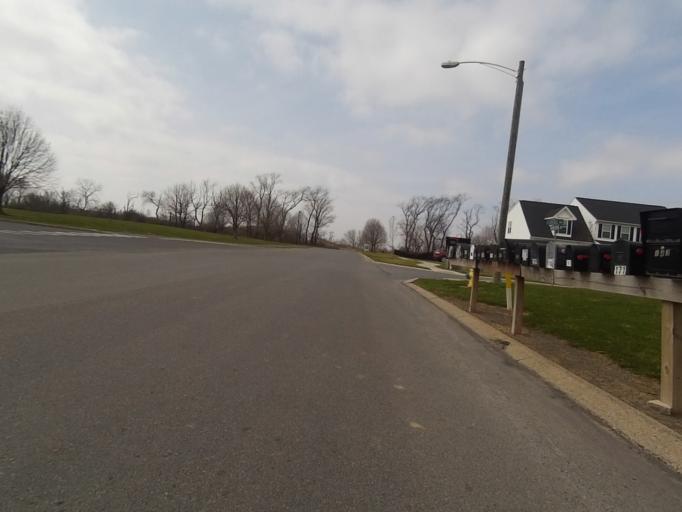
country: US
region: Pennsylvania
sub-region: Centre County
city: Boalsburg
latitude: 40.7875
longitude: -77.8057
